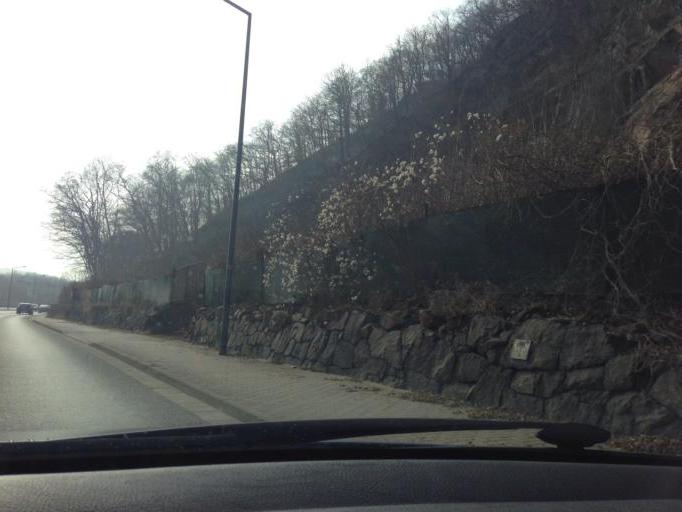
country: DE
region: Saxony
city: Freital
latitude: 51.0194
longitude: 13.6776
